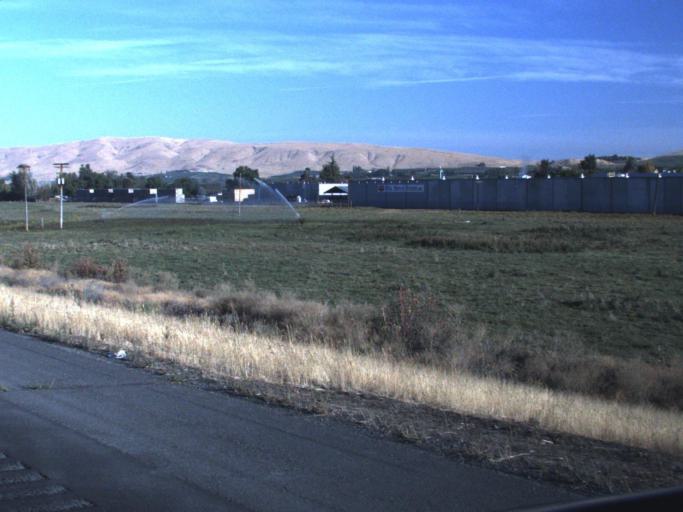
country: US
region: Washington
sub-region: Yakima County
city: Wapato
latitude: 46.4523
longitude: -120.3622
